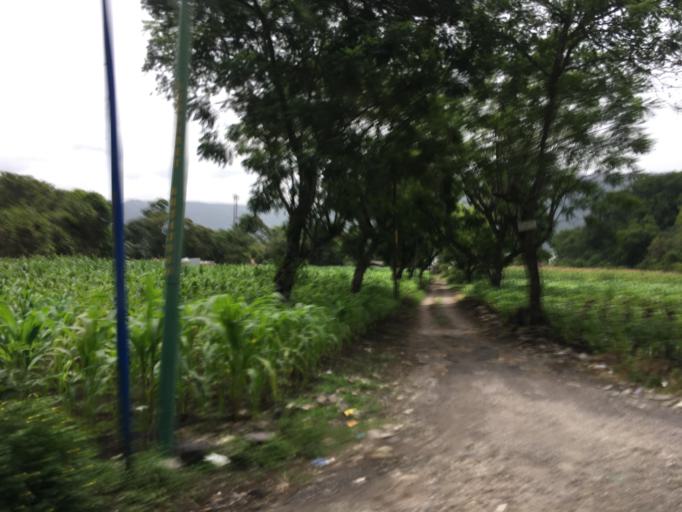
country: GT
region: Guatemala
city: Villa Canales
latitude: 14.4322
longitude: -90.5593
